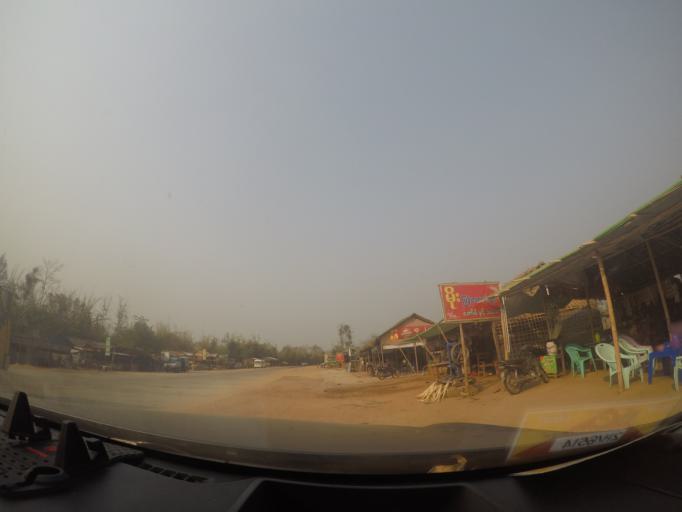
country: MM
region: Mandalay
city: Nay Pyi Taw
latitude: 19.9284
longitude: 95.9853
